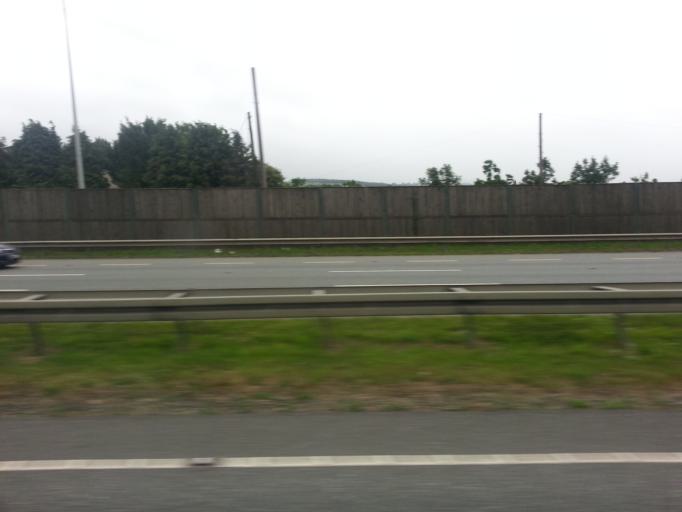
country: IE
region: Leinster
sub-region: Kildare
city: Kill
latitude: 53.2591
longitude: -6.5488
